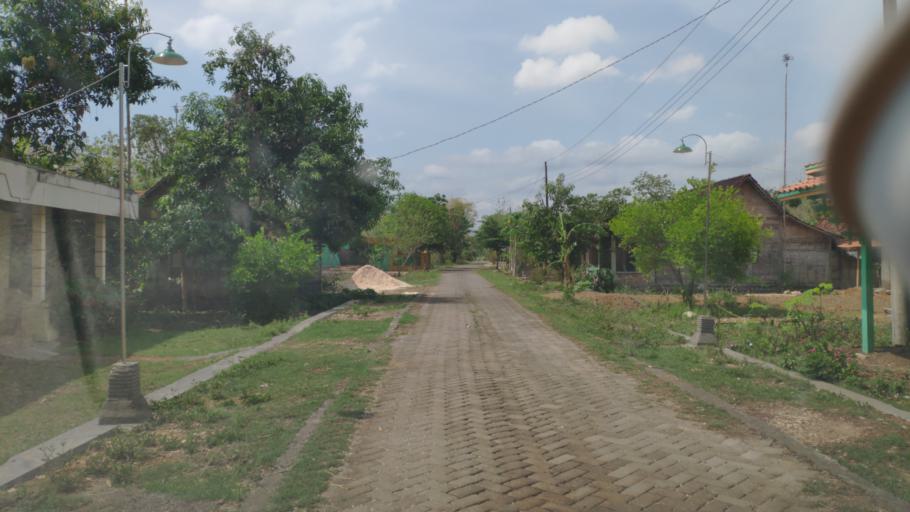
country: ID
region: Central Java
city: Balongrejo
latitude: -7.0135
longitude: 111.3697
